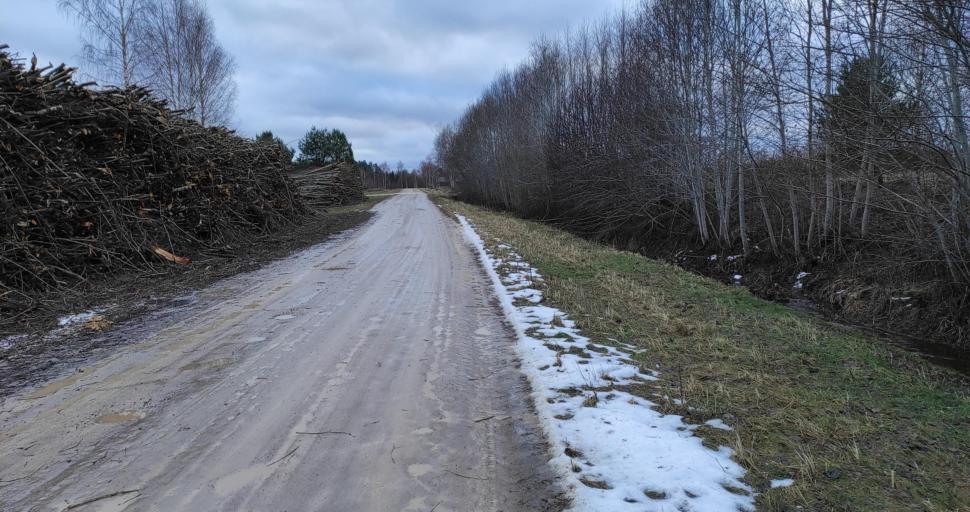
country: LV
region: Talsu Rajons
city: Stende
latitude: 57.0641
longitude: 22.2892
